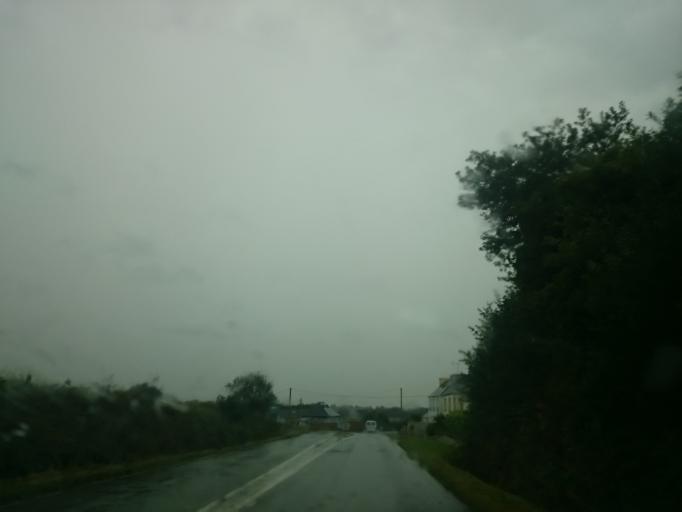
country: FR
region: Brittany
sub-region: Departement du Finistere
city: Plabennec
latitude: 48.5169
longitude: -4.4051
